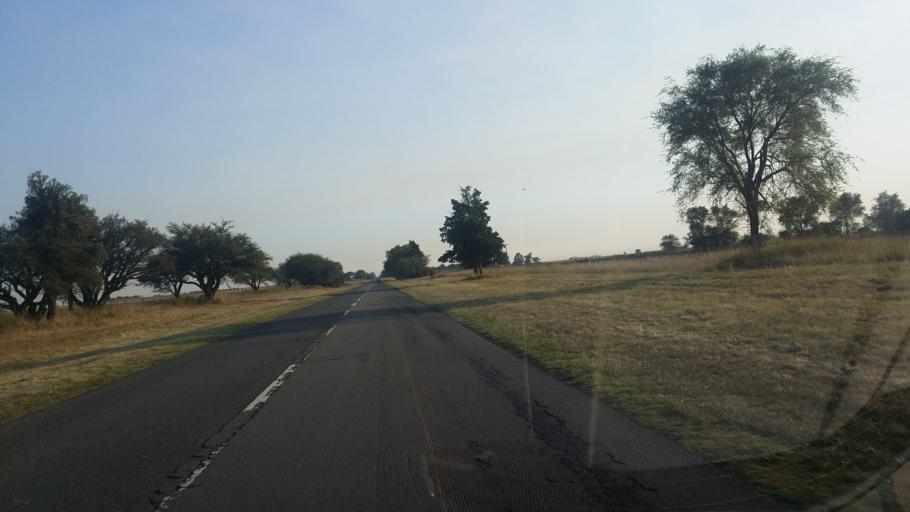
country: AR
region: La Pampa
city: Winifreda
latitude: -36.2132
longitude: -64.2782
